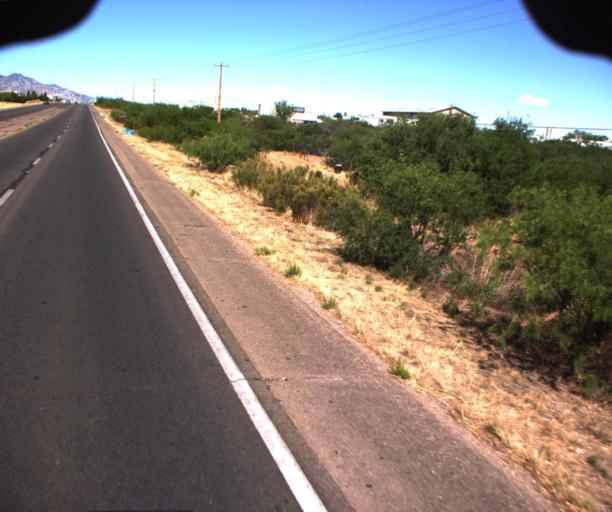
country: US
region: Arizona
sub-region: Cochise County
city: Sierra Vista
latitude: 31.5547
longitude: -110.2350
